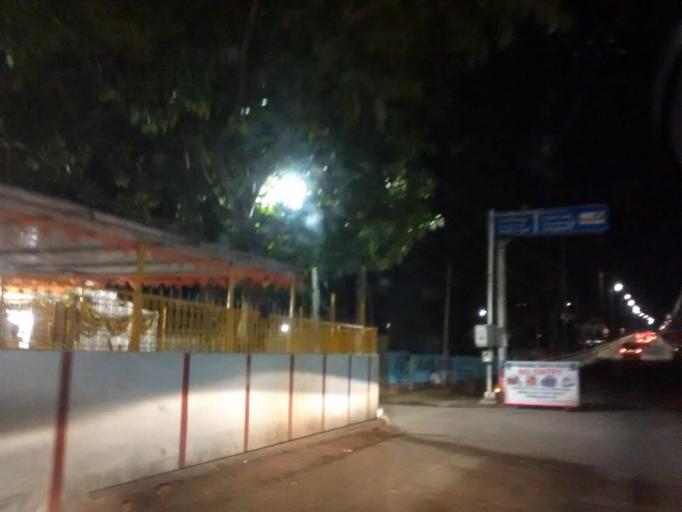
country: IN
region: Telangana
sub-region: Hyderabad
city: Hyderabad
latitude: 17.3234
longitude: 78.4296
